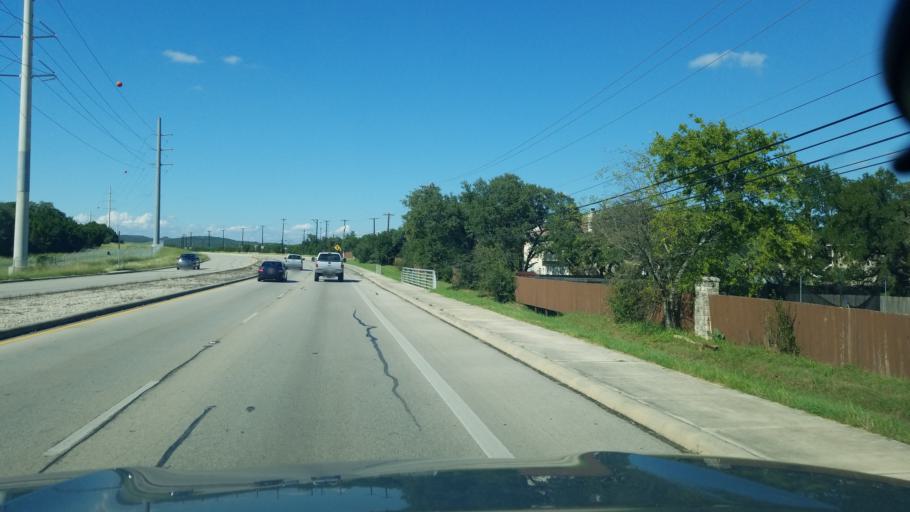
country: US
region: Texas
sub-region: Bexar County
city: Hollywood Park
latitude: 29.6482
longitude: -98.5184
